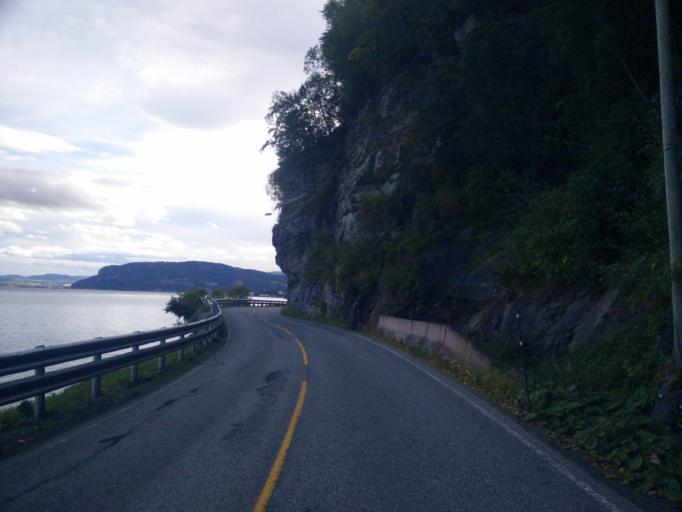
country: NO
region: Sor-Trondelag
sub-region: Skaun
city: Borsa
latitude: 63.3271
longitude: 10.1092
